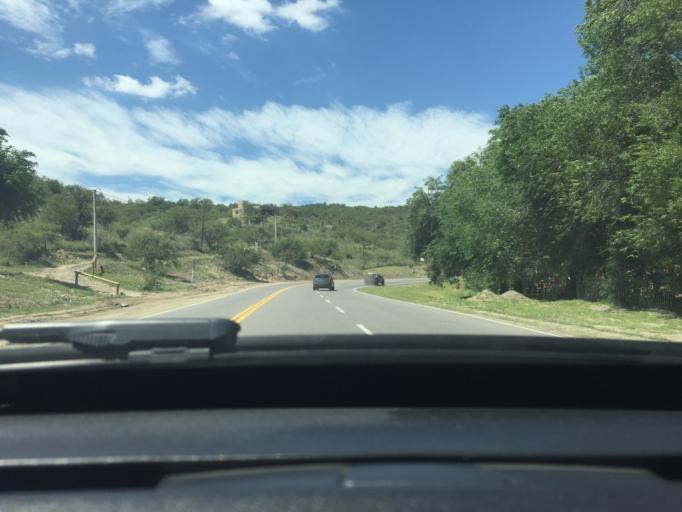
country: AR
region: Cordoba
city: Alta Gracia
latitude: -31.7390
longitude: -64.4531
